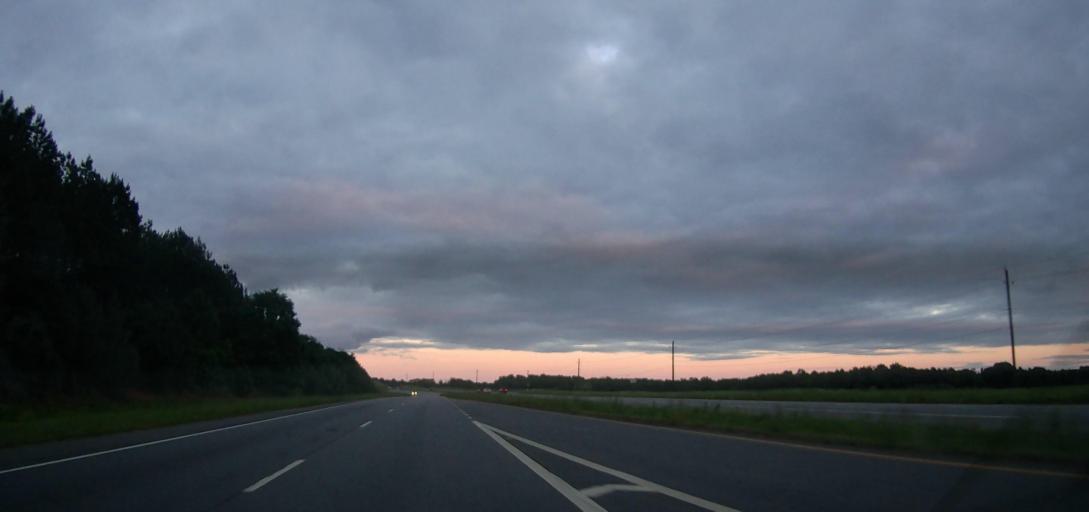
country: US
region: Georgia
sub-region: Jackson County
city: Arcade
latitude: 34.0626
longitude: -83.5271
